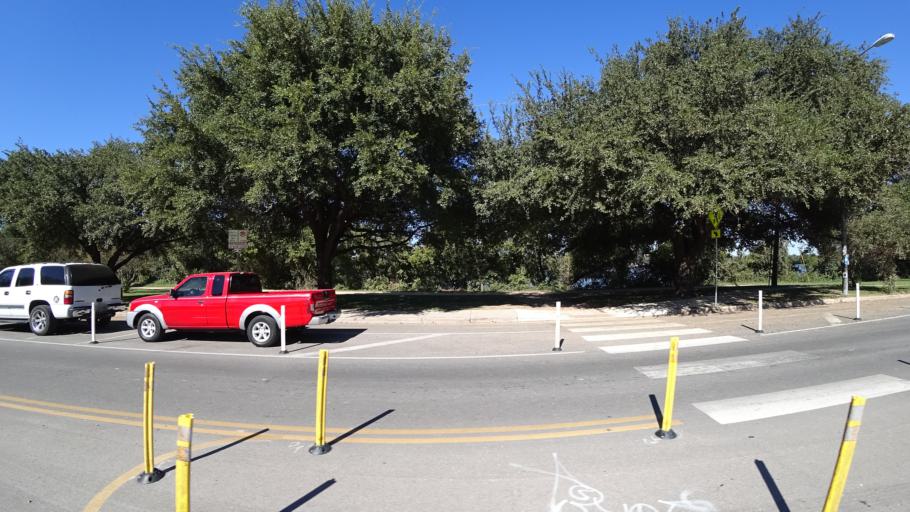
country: US
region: Texas
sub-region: Travis County
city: Austin
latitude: 30.2444
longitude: -97.7224
